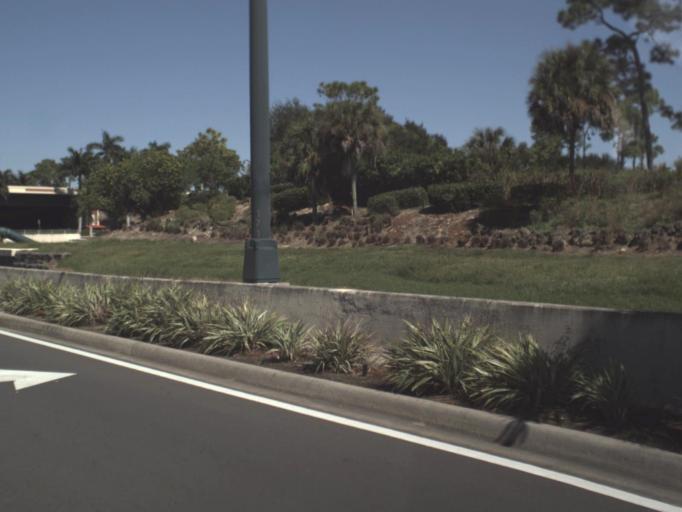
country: US
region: Florida
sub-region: Collier County
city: Naples
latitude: 26.1726
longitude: -81.7669
